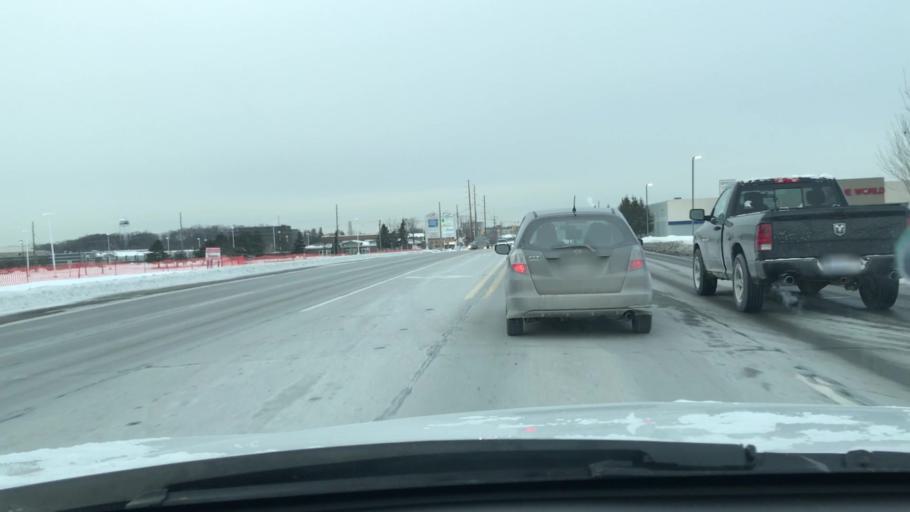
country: US
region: Michigan
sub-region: Oakland County
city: Sylvan Lake
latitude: 42.6451
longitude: -83.3262
